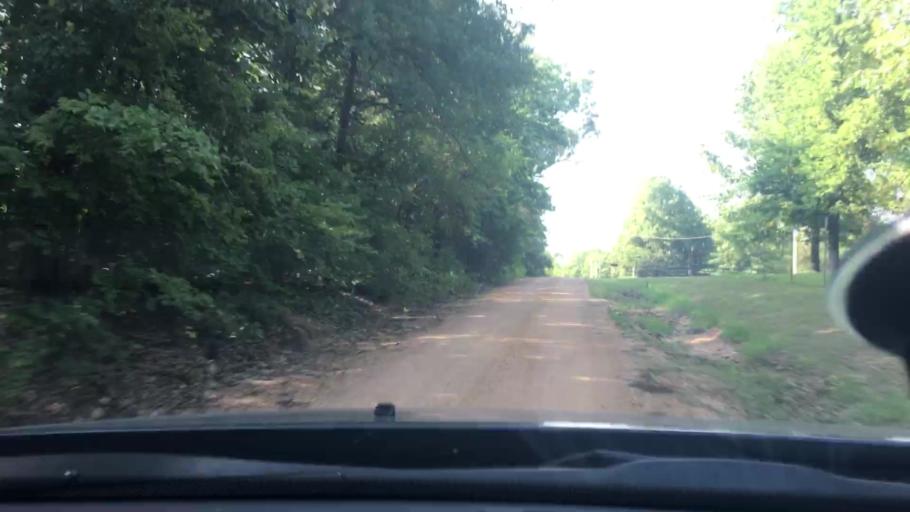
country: US
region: Oklahoma
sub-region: Johnston County
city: Tishomingo
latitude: 34.2103
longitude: -96.6187
